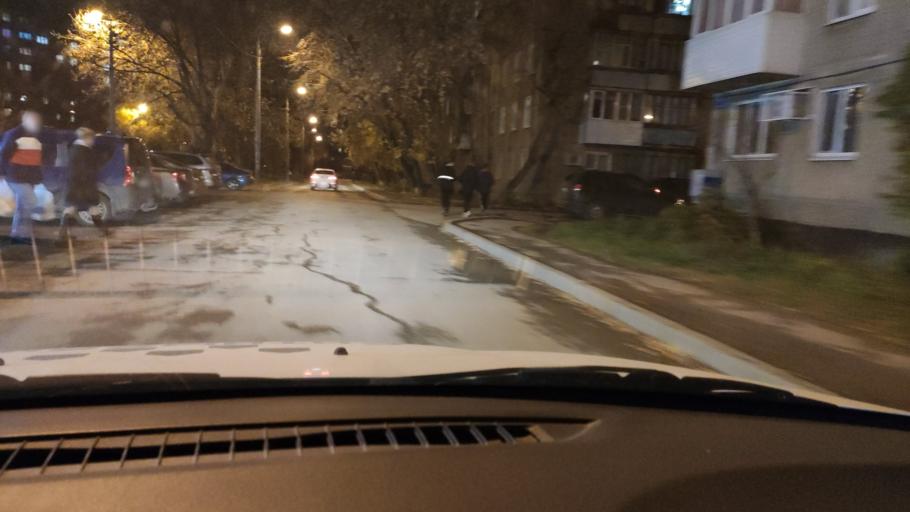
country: RU
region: Perm
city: Perm
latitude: 57.9663
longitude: 56.1942
